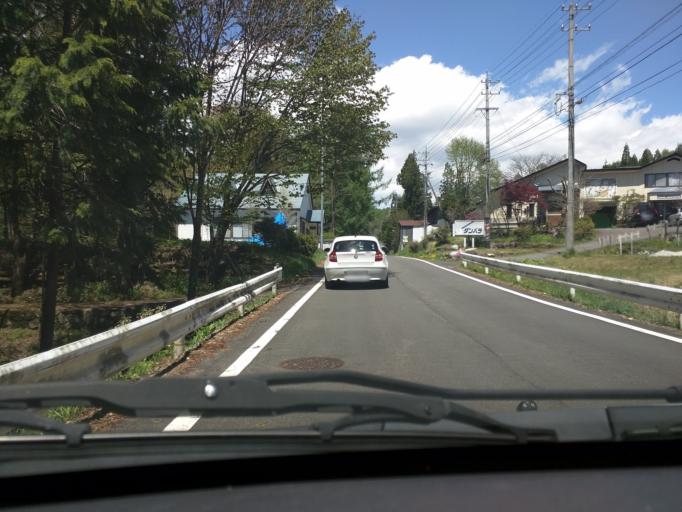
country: JP
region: Nagano
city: Nagano-shi
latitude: 36.7156
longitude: 138.0858
